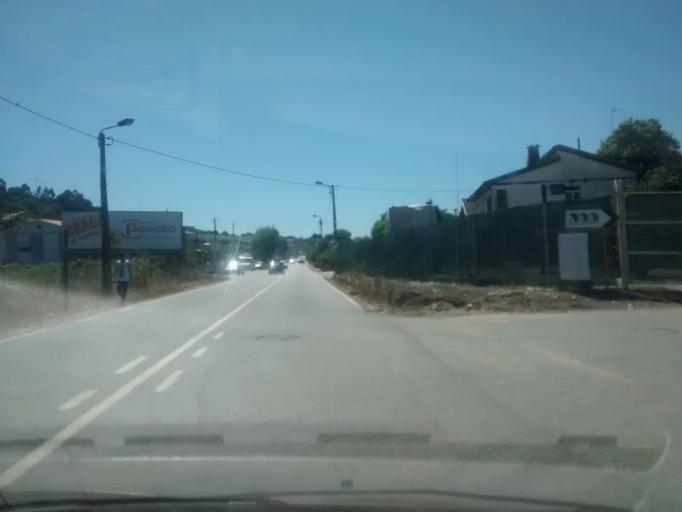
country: PT
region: Braga
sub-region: Braga
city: Oliveira
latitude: 41.5341
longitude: -8.5029
